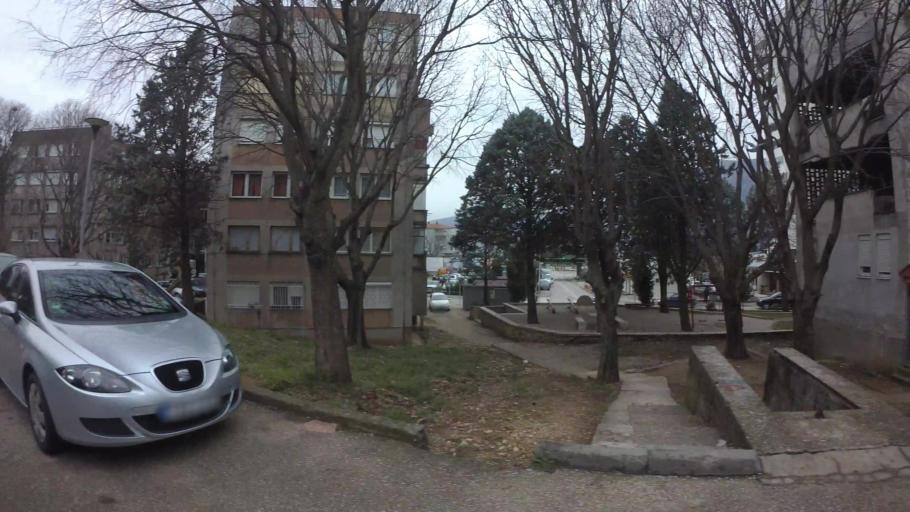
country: BA
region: Federation of Bosnia and Herzegovina
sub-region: Hercegovacko-Bosanski Kanton
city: Mostar
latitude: 43.3558
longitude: 17.8142
